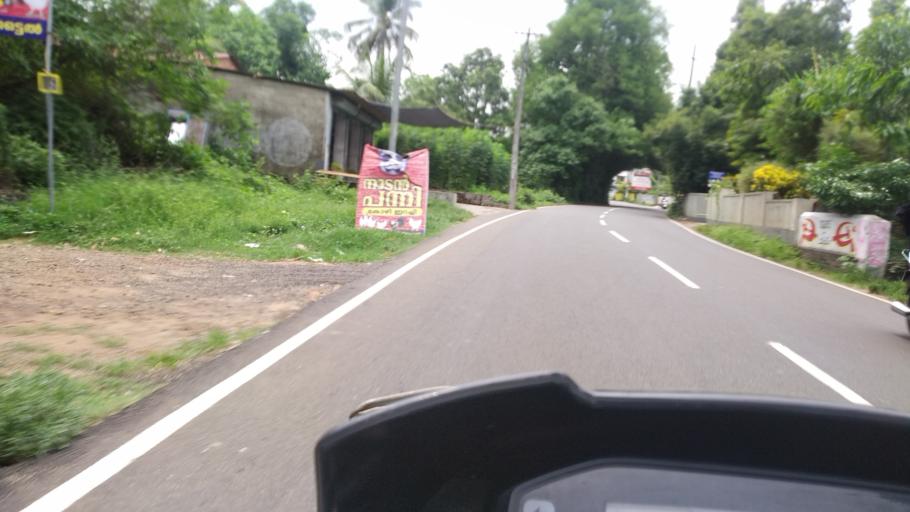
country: IN
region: Kerala
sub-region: Ernakulam
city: Aluva
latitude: 10.1559
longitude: 76.3165
